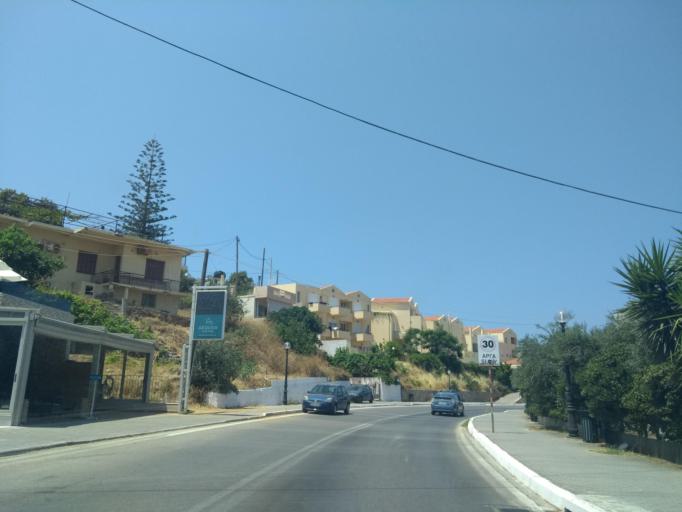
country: GR
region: Crete
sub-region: Nomos Chanias
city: Daratsos
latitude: 35.5078
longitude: 23.9882
